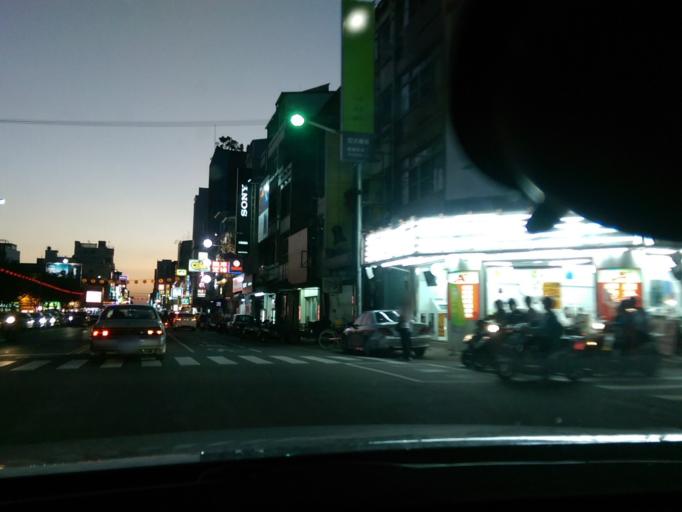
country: TW
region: Taiwan
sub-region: Chiayi
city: Jiayi Shi
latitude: 23.4762
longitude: 120.4518
